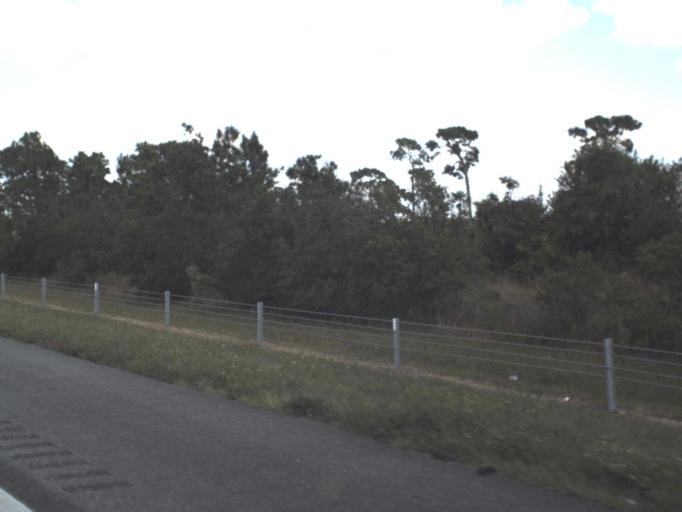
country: US
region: Florida
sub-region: Indian River County
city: Fellsmere
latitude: 27.8136
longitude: -81.0017
